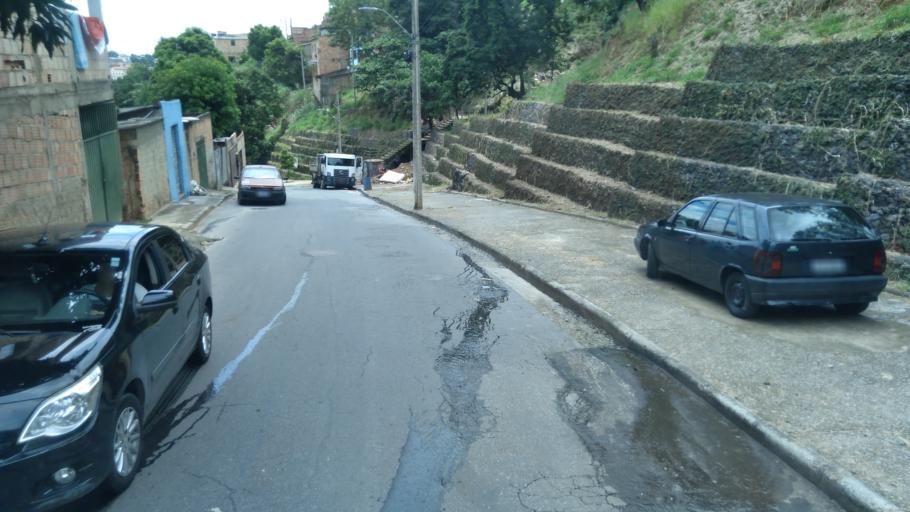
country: BR
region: Minas Gerais
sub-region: Belo Horizonte
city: Belo Horizonte
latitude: -19.8506
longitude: -43.8924
